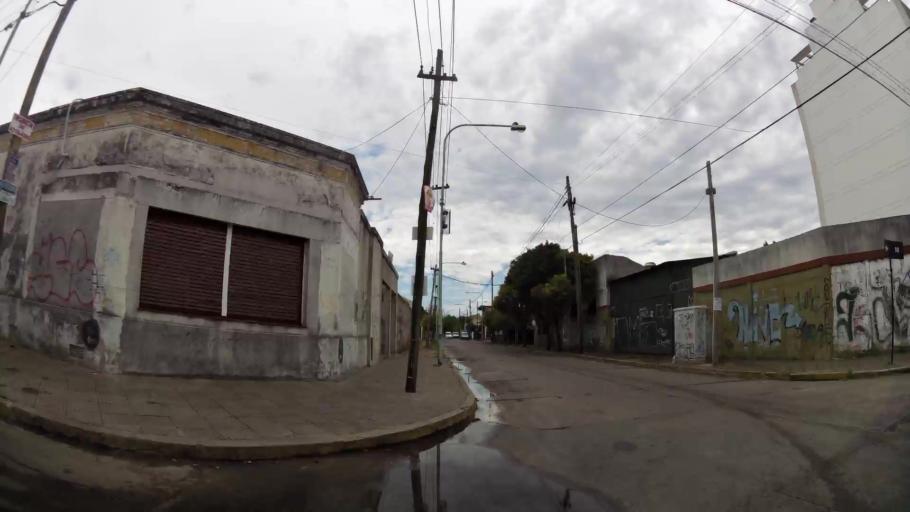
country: AR
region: Buenos Aires
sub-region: Partido de Quilmes
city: Quilmes
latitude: -34.7591
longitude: -58.2150
